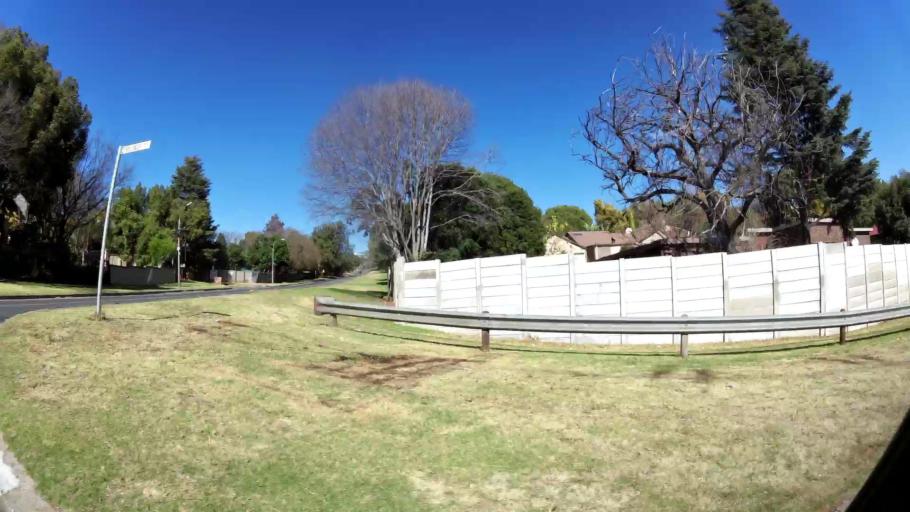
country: ZA
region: Gauteng
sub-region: City of Johannesburg Metropolitan Municipality
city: Roodepoort
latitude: -26.1208
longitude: 27.8677
